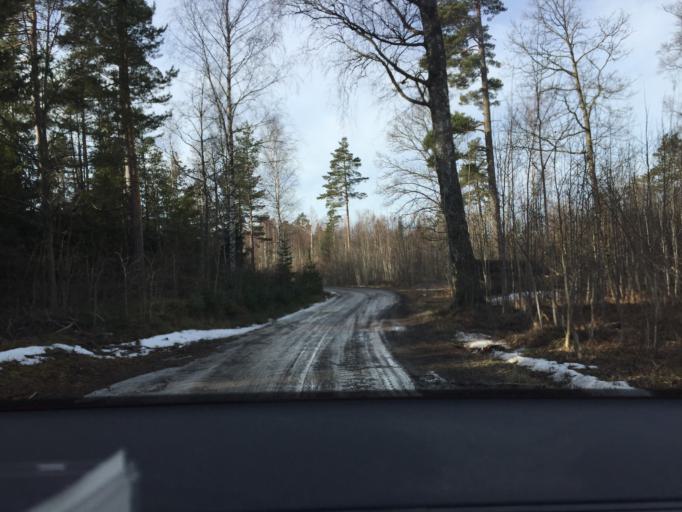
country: SE
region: OErebro
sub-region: Orebro Kommun
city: Odensbacken
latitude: 59.1174
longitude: 15.4423
